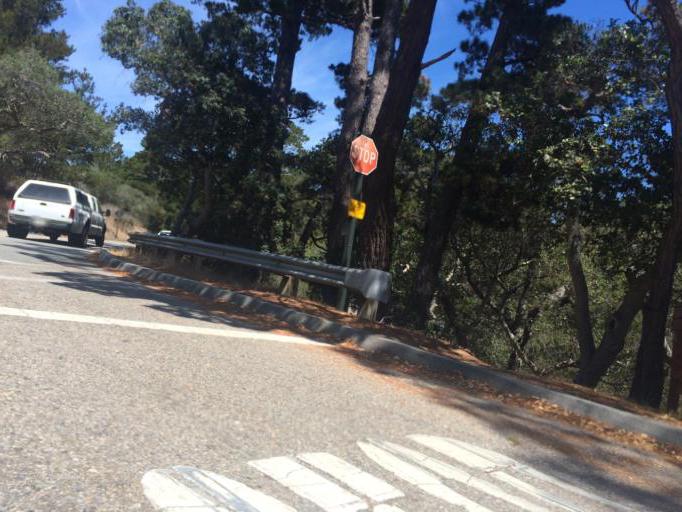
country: US
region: California
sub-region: Monterey County
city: Carmel-by-the-Sea
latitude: 36.5608
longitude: -121.9259
